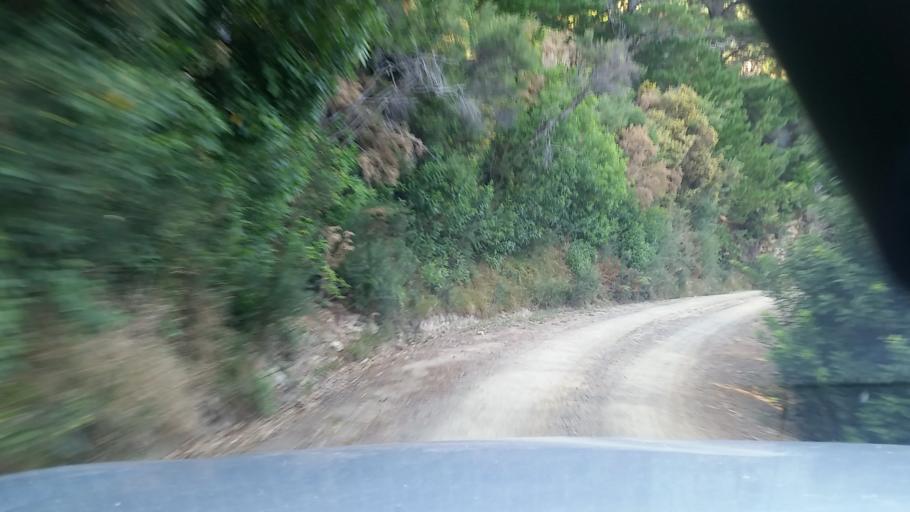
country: NZ
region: Marlborough
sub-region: Marlborough District
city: Picton
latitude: -41.3011
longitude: 174.1782
